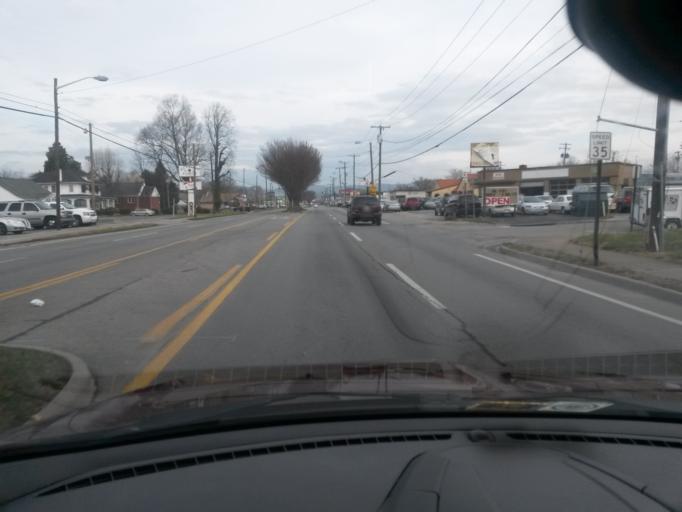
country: US
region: Virginia
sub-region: Roanoke County
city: Hollins
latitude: 37.3089
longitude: -79.9486
